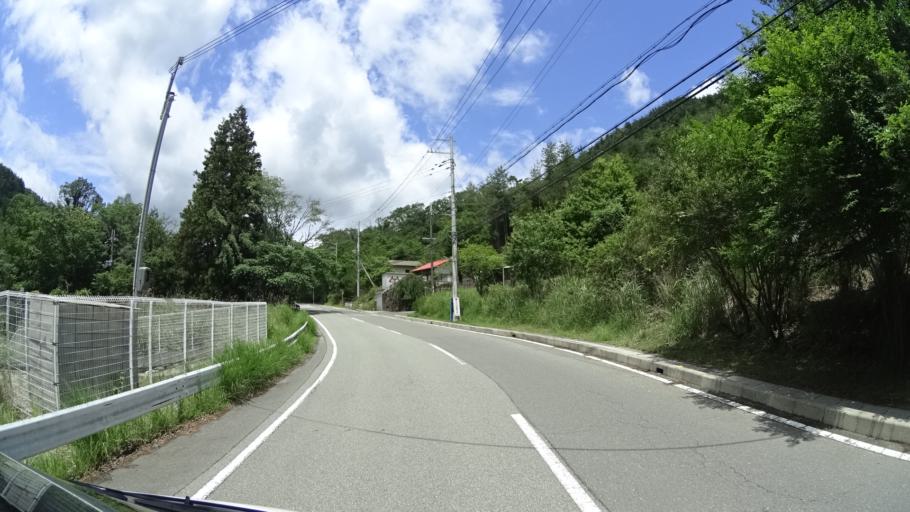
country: JP
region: Kyoto
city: Kameoka
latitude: 35.0192
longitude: 135.4082
